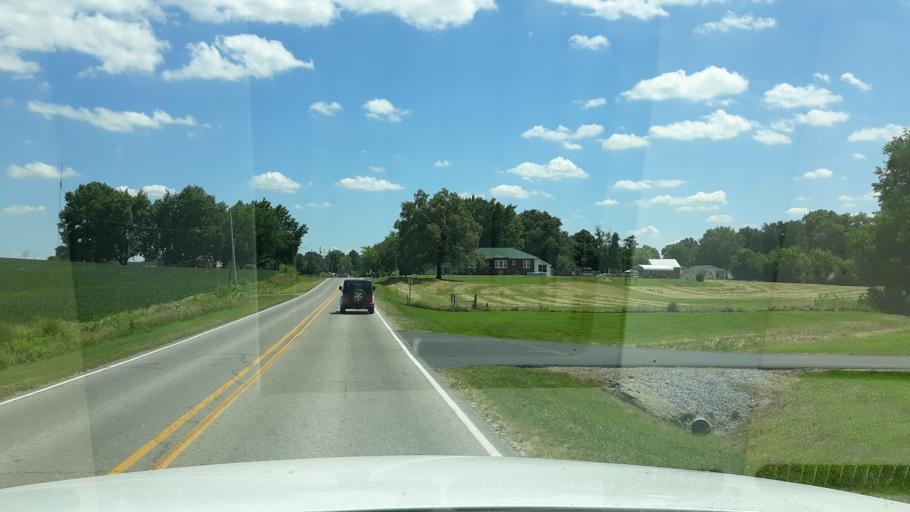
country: US
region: Illinois
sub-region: Saline County
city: Harrisburg
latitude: 37.8459
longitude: -88.6054
